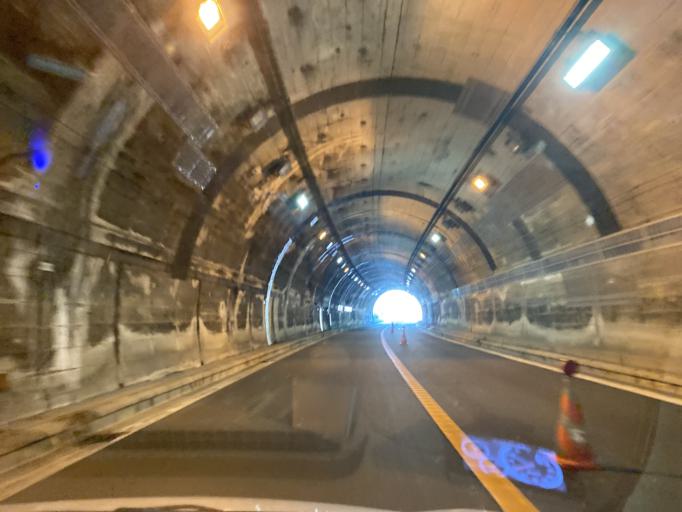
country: JP
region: Wakayama
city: Iwade
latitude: 34.3049
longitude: 135.2704
